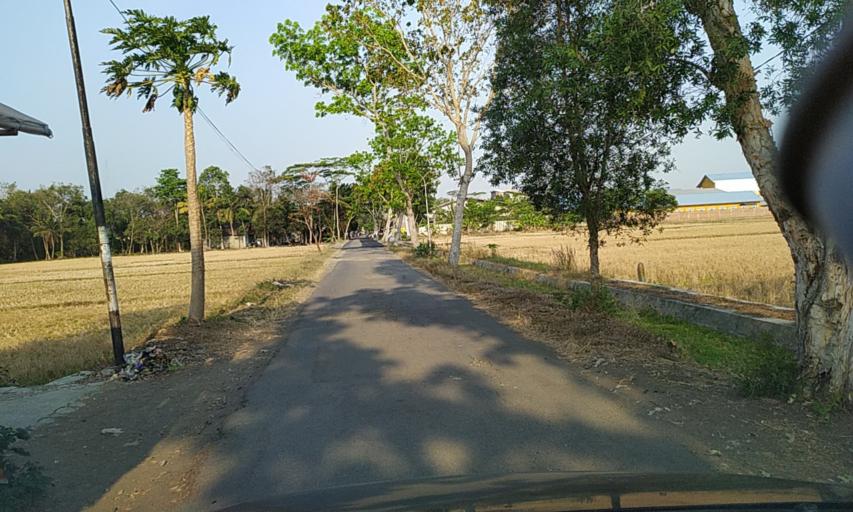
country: ID
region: Central Java
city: Sidareja
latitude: -7.4869
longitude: 108.7955
